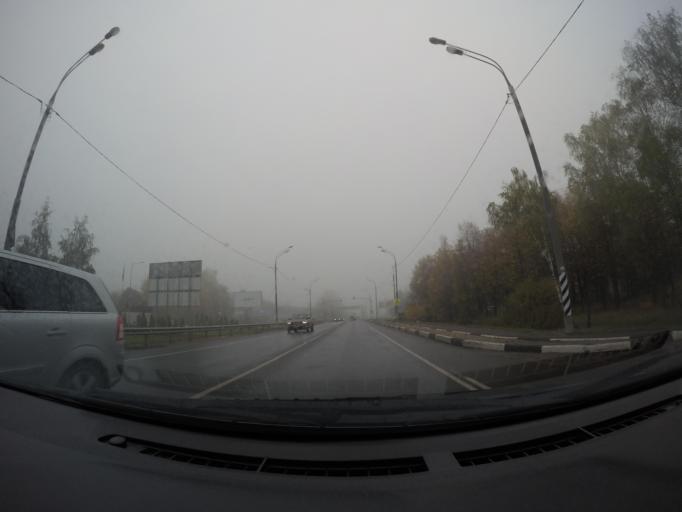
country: RU
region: Moskovskaya
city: Ruza
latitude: 55.7058
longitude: 36.2080
